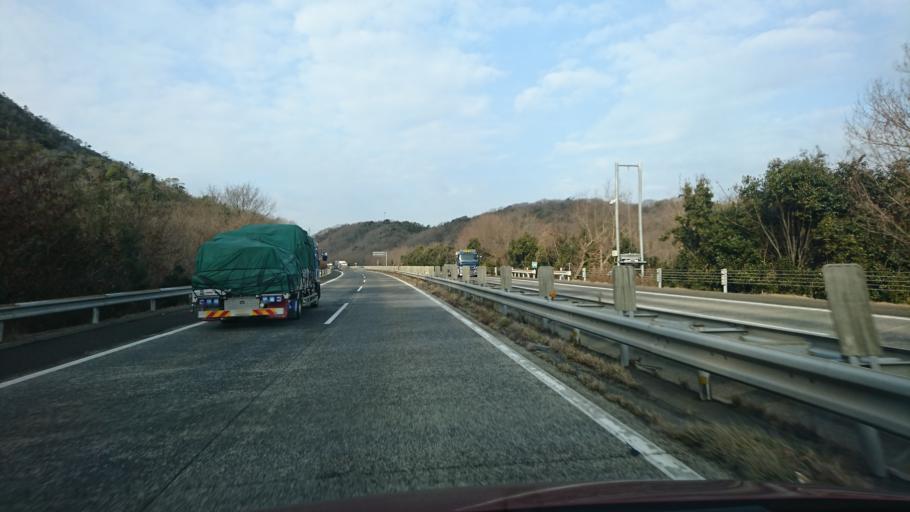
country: JP
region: Hyogo
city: Kariya
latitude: 34.7831
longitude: 134.2829
